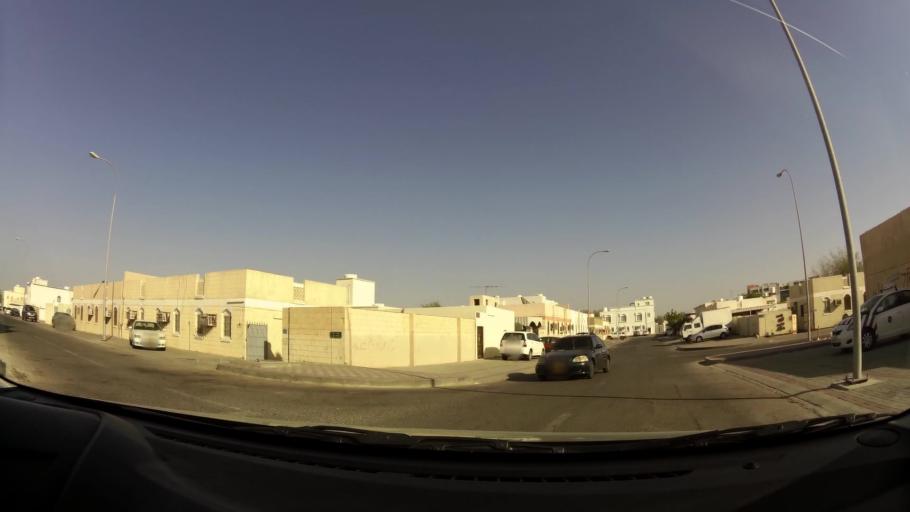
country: OM
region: Muhafazat Masqat
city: As Sib al Jadidah
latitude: 23.6189
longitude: 58.1910
